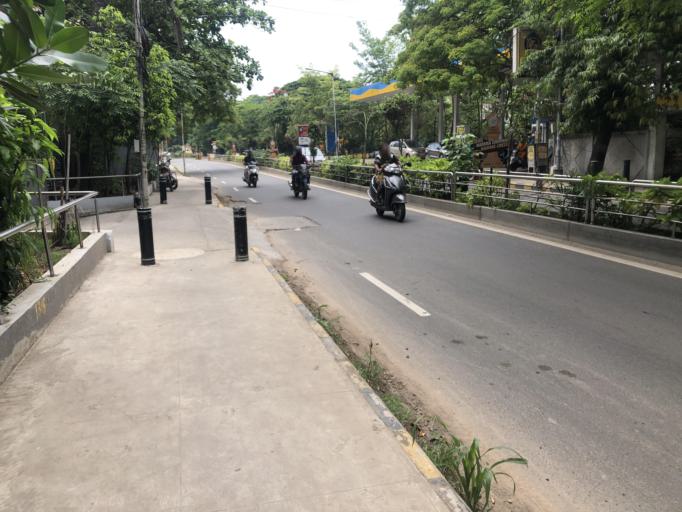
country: IN
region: Tamil Nadu
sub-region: Chennai
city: Gandhi Nagar
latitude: 13.0283
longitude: 80.2508
